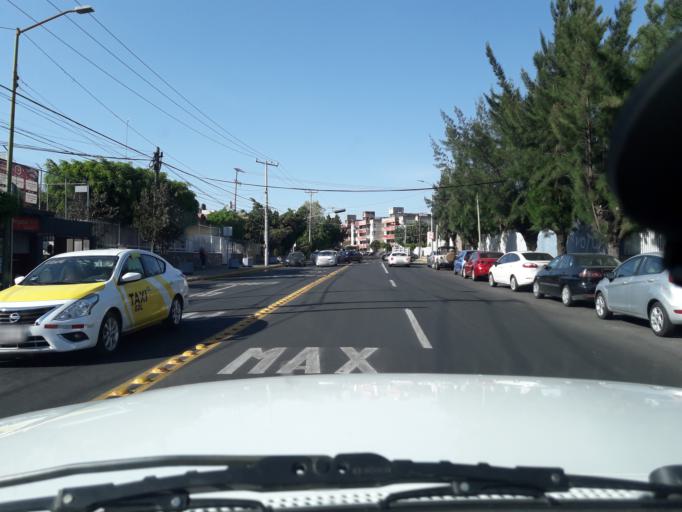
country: MX
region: Jalisco
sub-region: Zapopan
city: Zapopan
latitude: 20.6935
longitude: -103.3517
